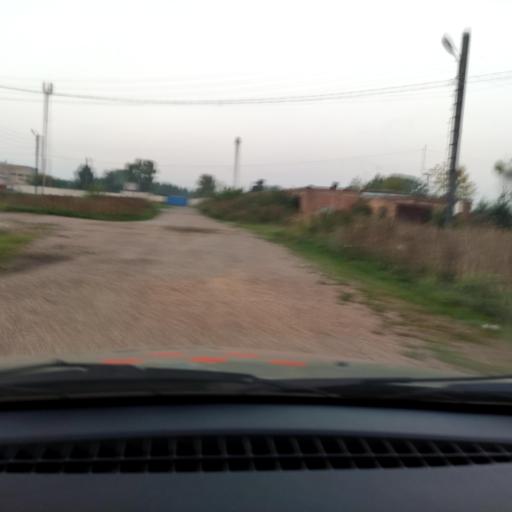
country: RU
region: Bashkortostan
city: Ufa
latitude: 54.8211
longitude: 56.1680
